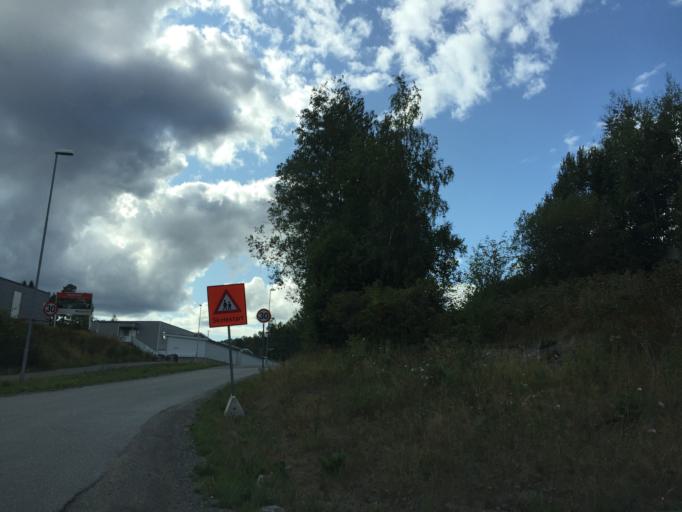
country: NO
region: Ostfold
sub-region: Askim
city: Askim
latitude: 59.5915
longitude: 11.1335
